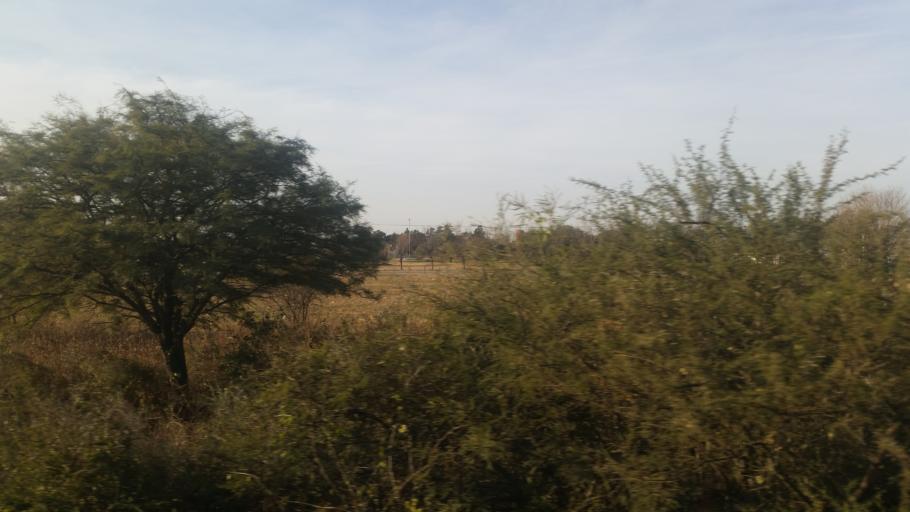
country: AR
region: Cordoba
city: Toledo
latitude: -31.5592
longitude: -64.0063
